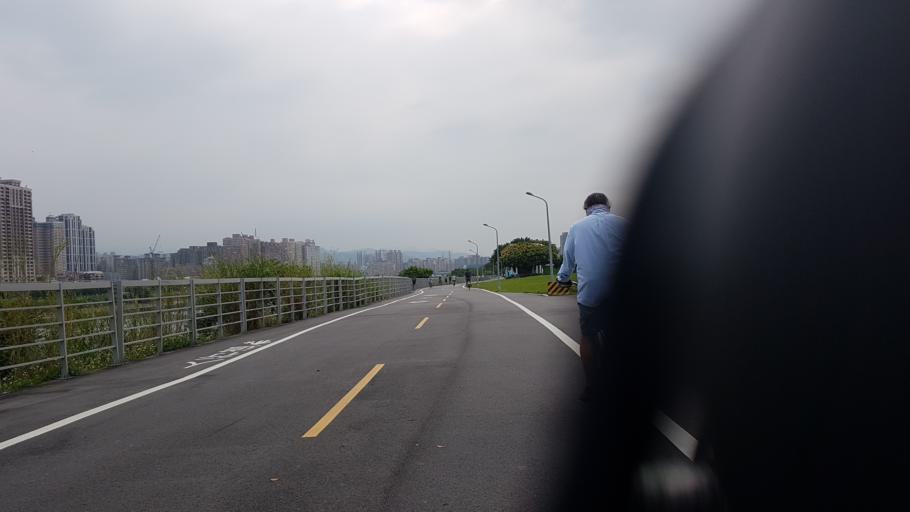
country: TW
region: Taipei
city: Taipei
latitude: 25.0210
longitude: 121.5069
